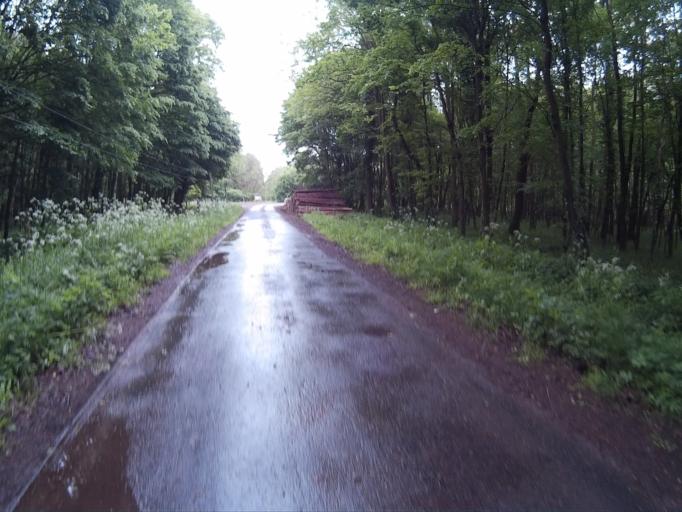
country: HU
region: Veszprem
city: Sumeg
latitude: 46.9293
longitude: 17.2991
